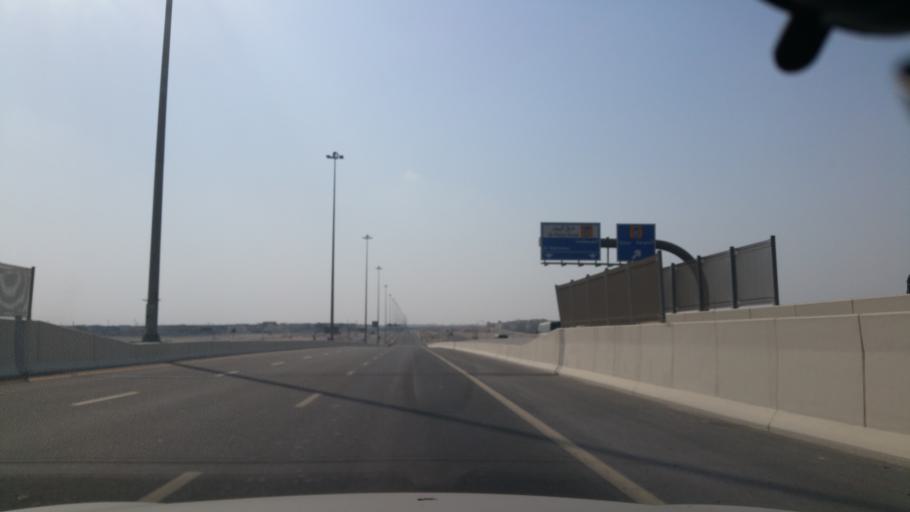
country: QA
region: Baladiyat Umm Salal
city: Umm Salal `Ali
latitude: 25.4571
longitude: 51.4778
